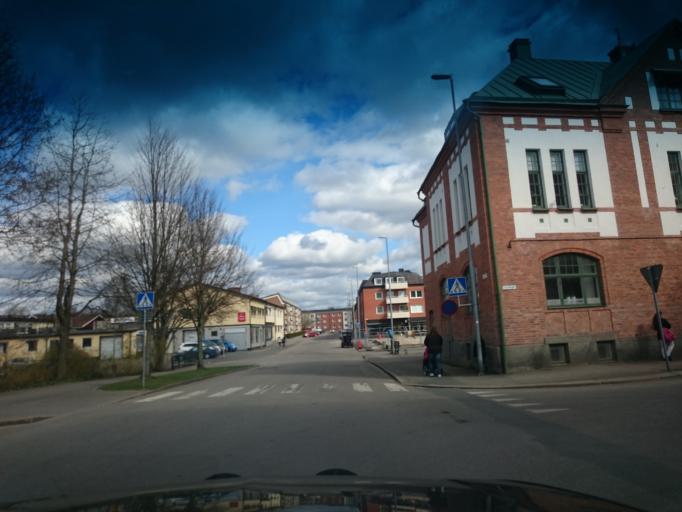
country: SE
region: Joenkoeping
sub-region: Vetlanda Kommun
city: Vetlanda
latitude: 57.4271
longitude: 15.0872
